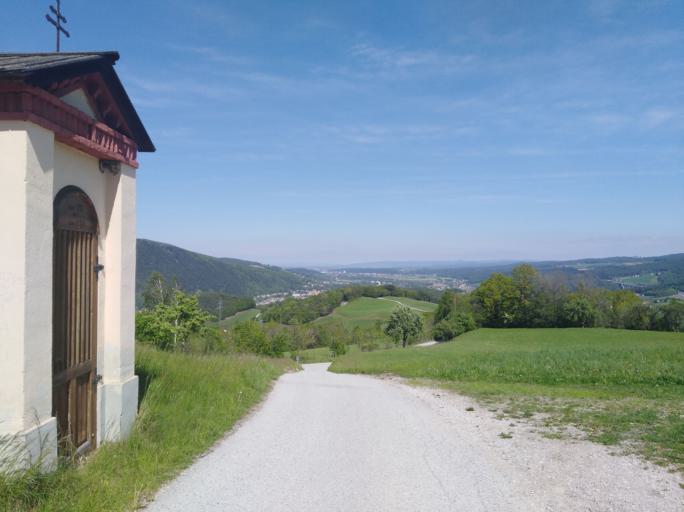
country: AT
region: Lower Austria
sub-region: Politischer Bezirk Neunkirchen
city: Gloggnitz
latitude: 47.6652
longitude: 15.9123
